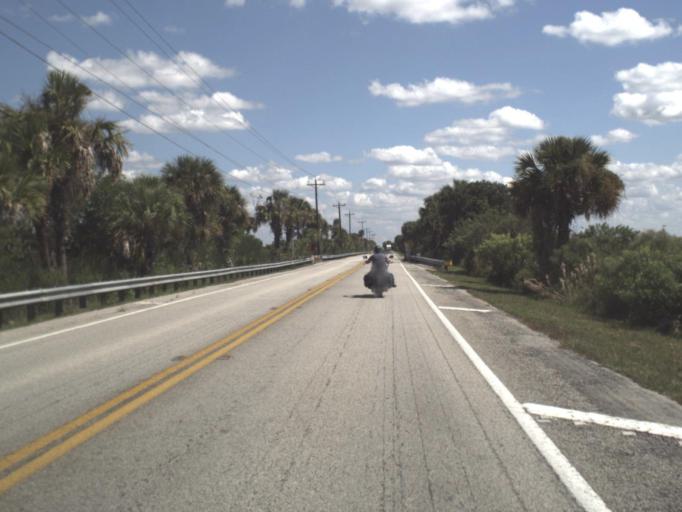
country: US
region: Florida
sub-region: Collier County
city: Marco
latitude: 25.9268
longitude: -81.4283
